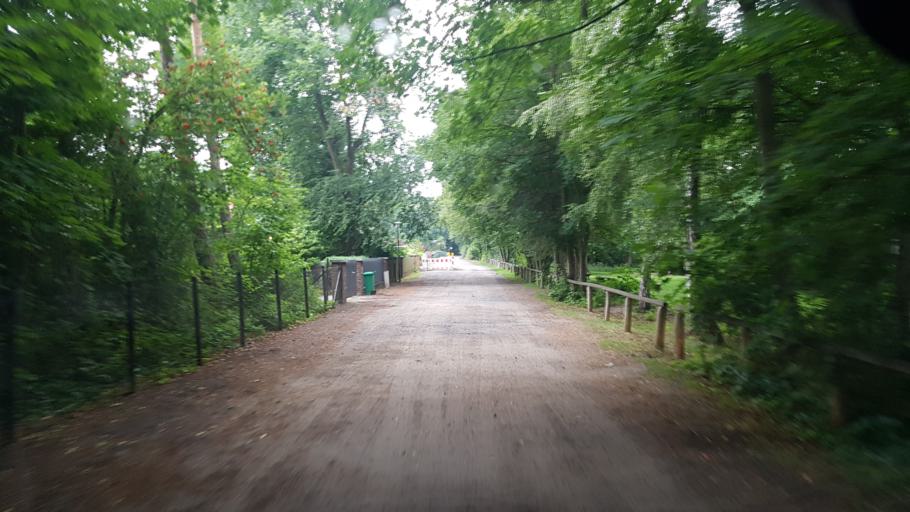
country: DE
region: Brandenburg
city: Gross Koris
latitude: 52.1724
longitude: 13.6984
